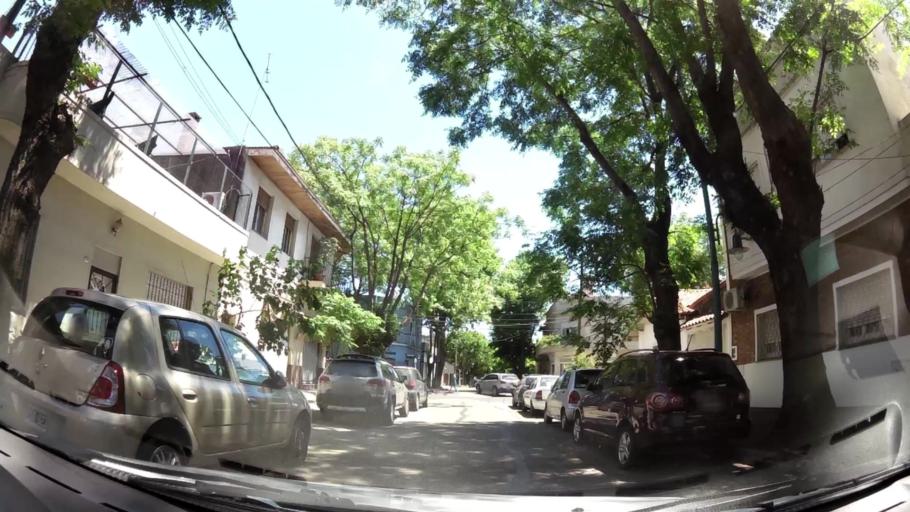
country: AR
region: Buenos Aires
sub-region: Partido de Vicente Lopez
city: Olivos
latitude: -34.5040
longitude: -58.4997
